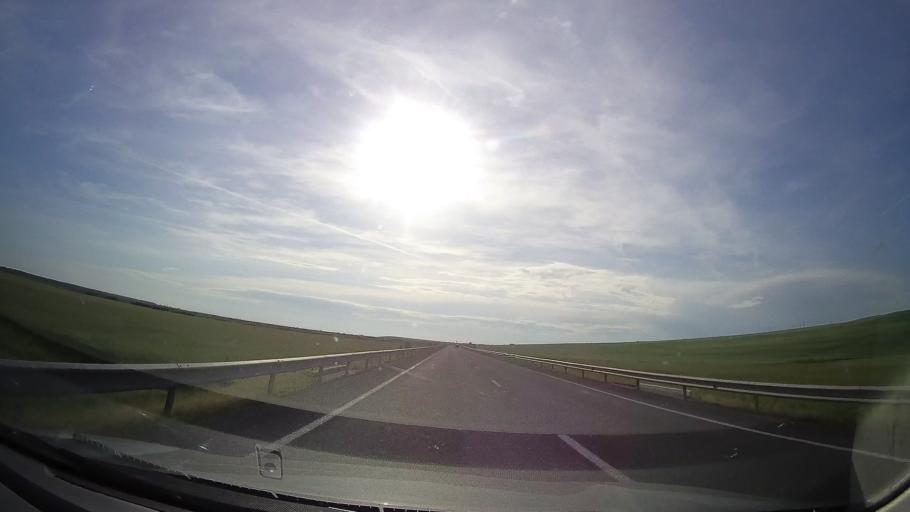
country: RO
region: Timis
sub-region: Comuna Topolovatu Mare
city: Topolovatu Mare
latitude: 45.7911
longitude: 21.5720
